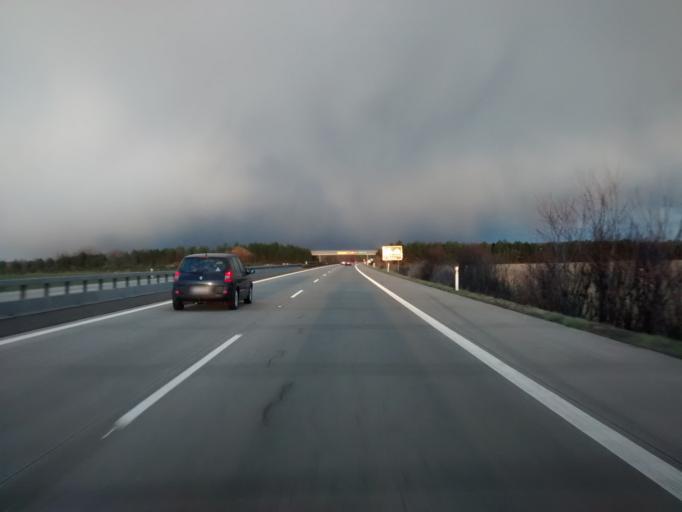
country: CZ
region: Central Bohemia
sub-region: Okres Nymburk
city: Podebrady
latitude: 50.1207
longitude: 15.0966
